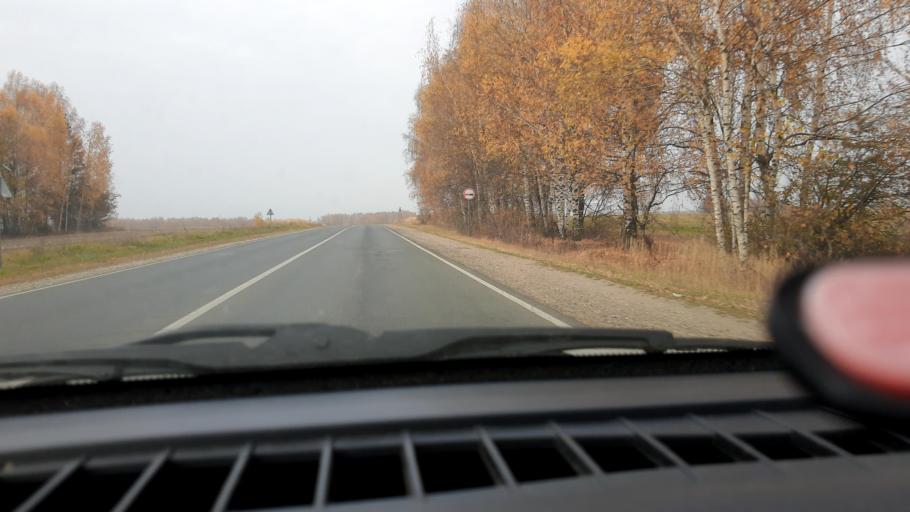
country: RU
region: Nizjnij Novgorod
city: Gorodets
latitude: 56.6256
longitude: 43.5468
